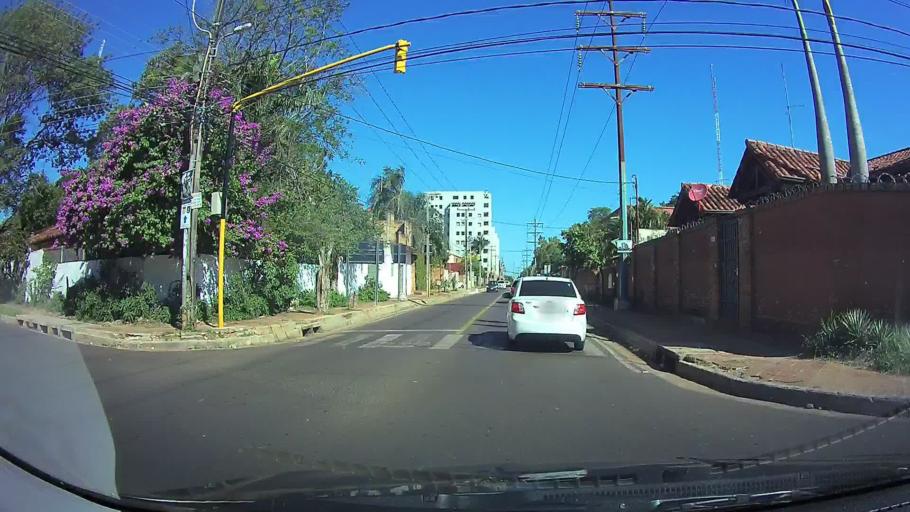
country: PY
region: Central
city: Fernando de la Mora
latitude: -25.3170
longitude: -57.5204
